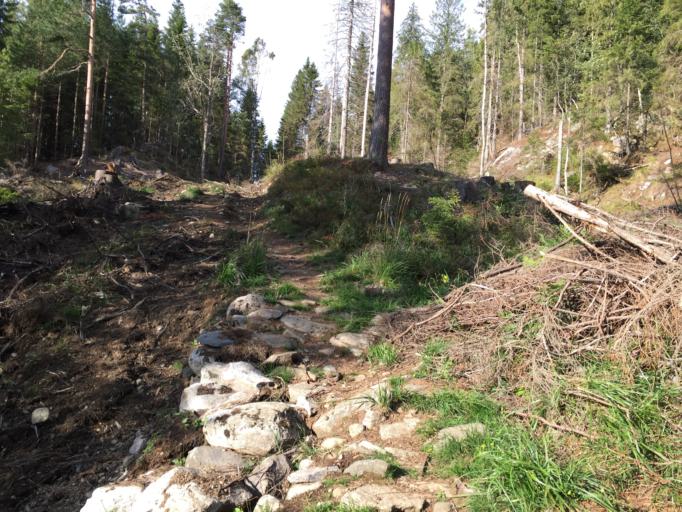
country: NO
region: Akershus
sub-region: Raelingen
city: Fjerdingby
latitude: 59.9202
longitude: 11.0316
